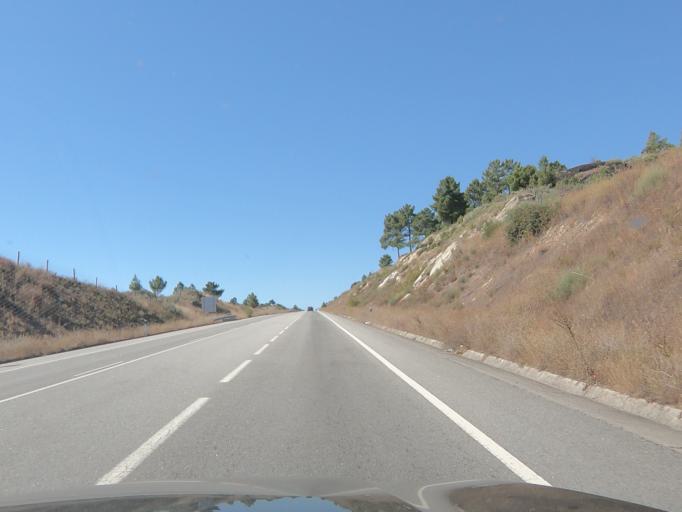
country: PT
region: Vila Real
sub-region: Valpacos
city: Valpacos
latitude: 41.5676
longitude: -7.2777
